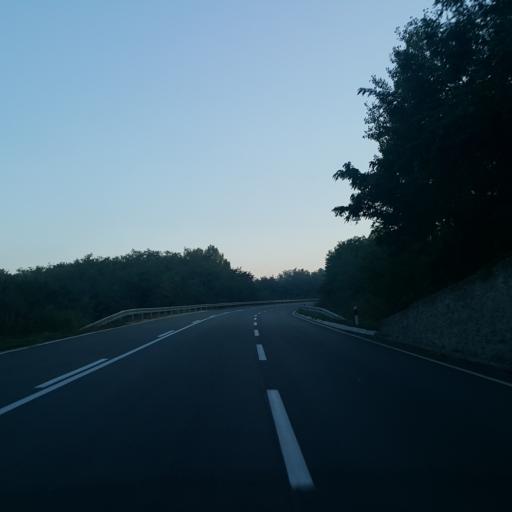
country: RS
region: Central Serbia
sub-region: Zajecarski Okrug
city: Zajecar
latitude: 43.9895
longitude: 22.2988
